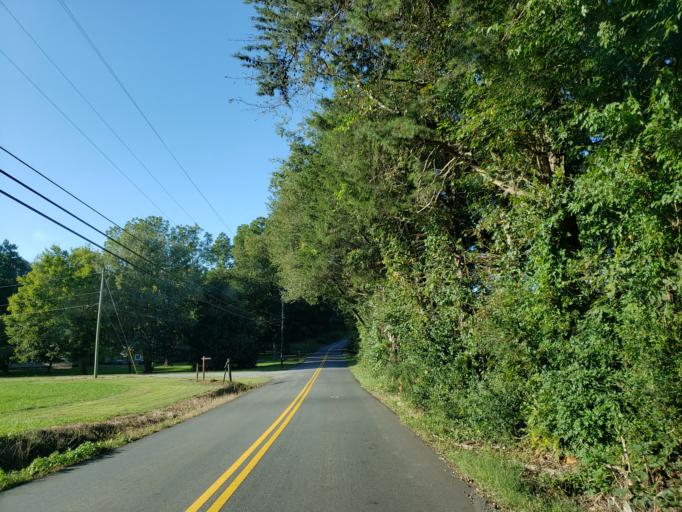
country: US
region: Georgia
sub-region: Bartow County
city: Rydal
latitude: 34.2860
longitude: -84.7513
